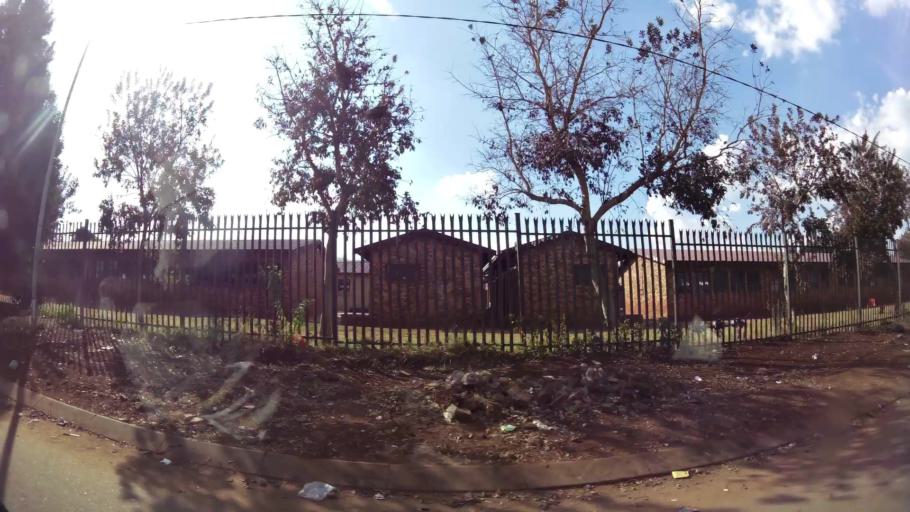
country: ZA
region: Gauteng
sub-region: City of Johannesburg Metropolitan Municipality
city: Soweto
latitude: -26.2192
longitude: 27.8602
